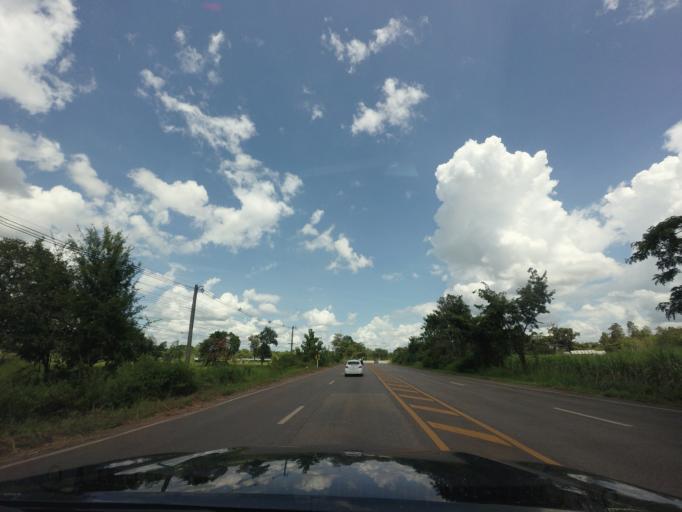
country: TH
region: Changwat Udon Thani
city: Ban Dung
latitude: 17.6853
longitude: 103.1964
